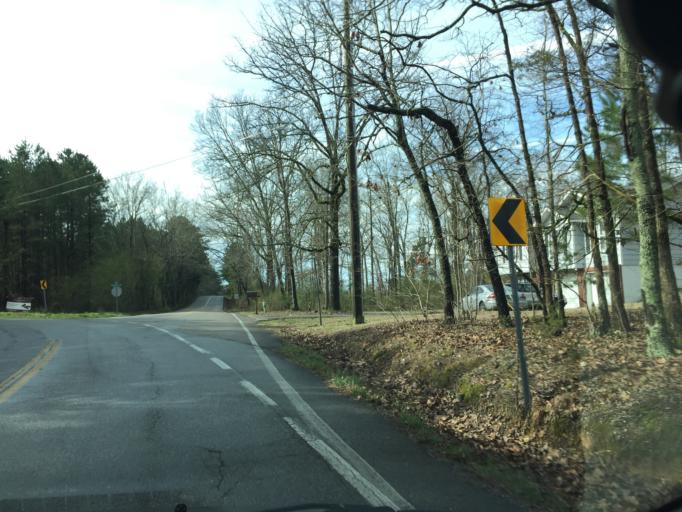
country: US
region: Tennessee
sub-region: Hamilton County
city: Collegedale
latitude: 35.0619
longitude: -85.1028
